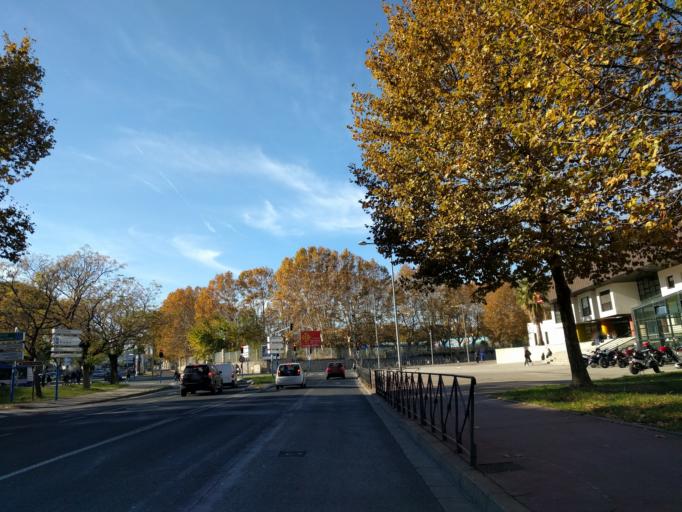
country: FR
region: Languedoc-Roussillon
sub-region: Departement de l'Herault
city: Montpellier
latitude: 43.6103
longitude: 3.8914
